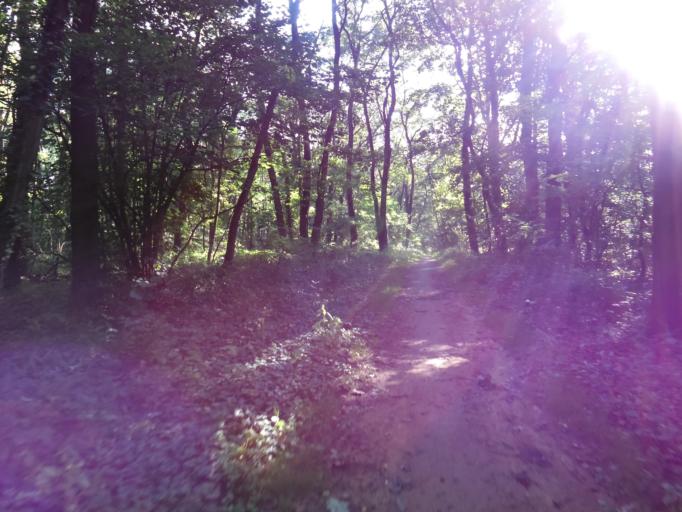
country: DE
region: Saxony-Anhalt
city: Coswig
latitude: 51.8823
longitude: 12.4968
